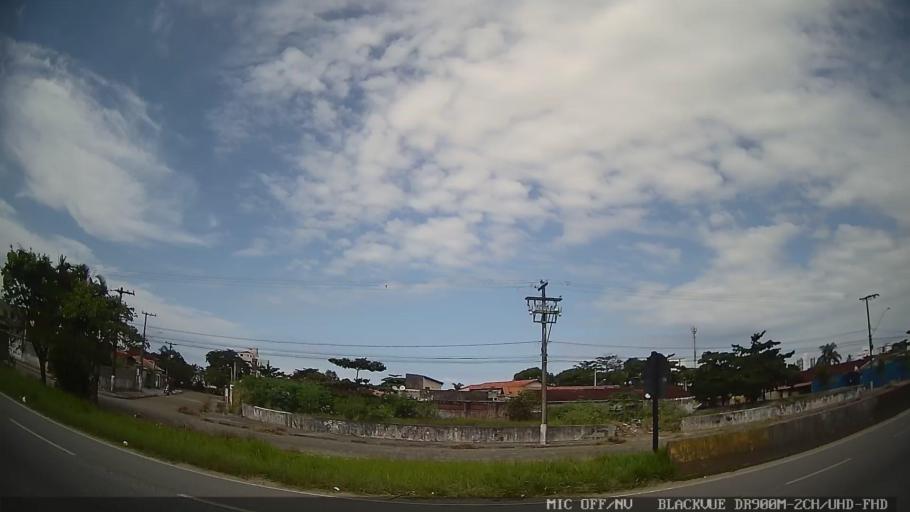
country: BR
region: Sao Paulo
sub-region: Mongagua
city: Mongagua
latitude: -24.1272
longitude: -46.6873
